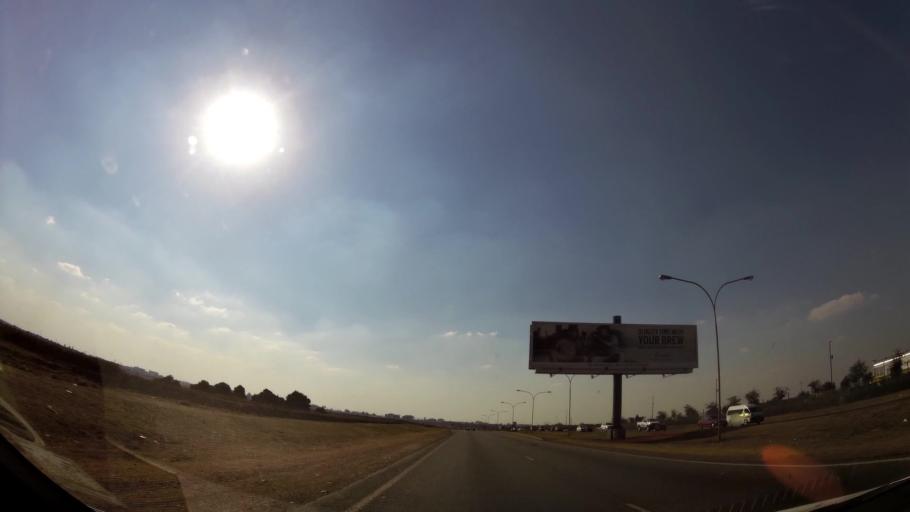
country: ZA
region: Gauteng
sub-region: Ekurhuleni Metropolitan Municipality
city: Brakpan
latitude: -26.2374
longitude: 28.3218
